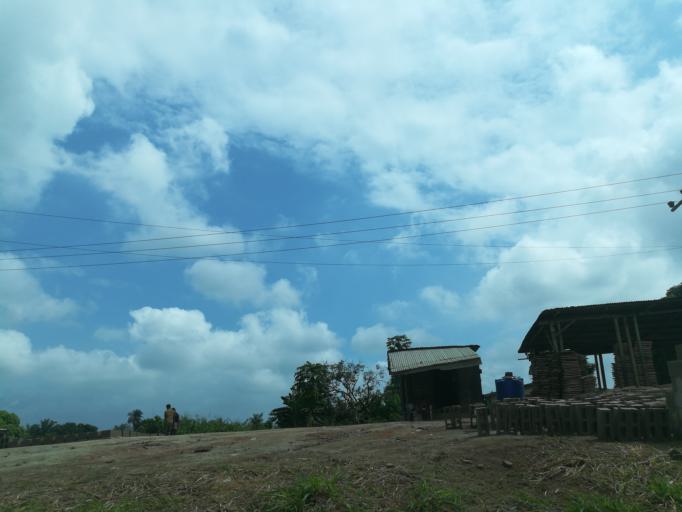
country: NG
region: Lagos
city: Ejirin
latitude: 6.6507
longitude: 3.7070
